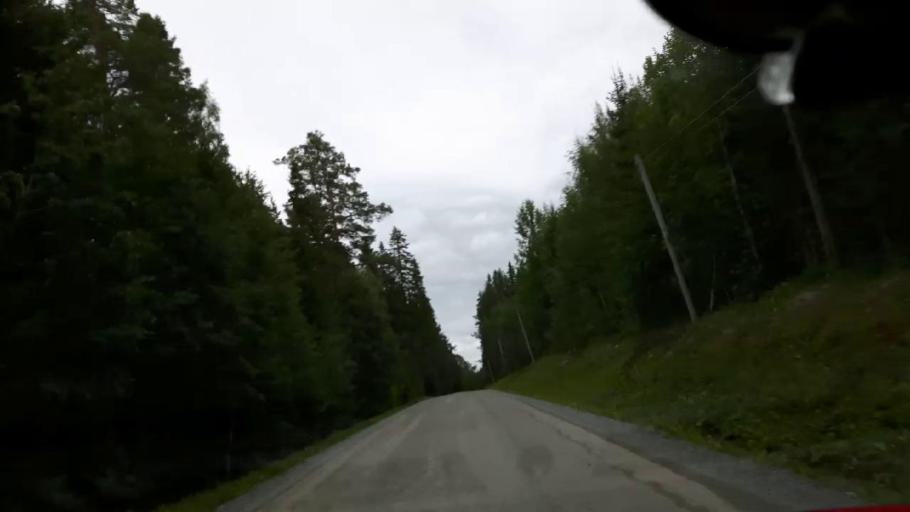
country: SE
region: Jaemtland
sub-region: Braecke Kommun
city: Braecke
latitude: 63.0897
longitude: 15.2577
